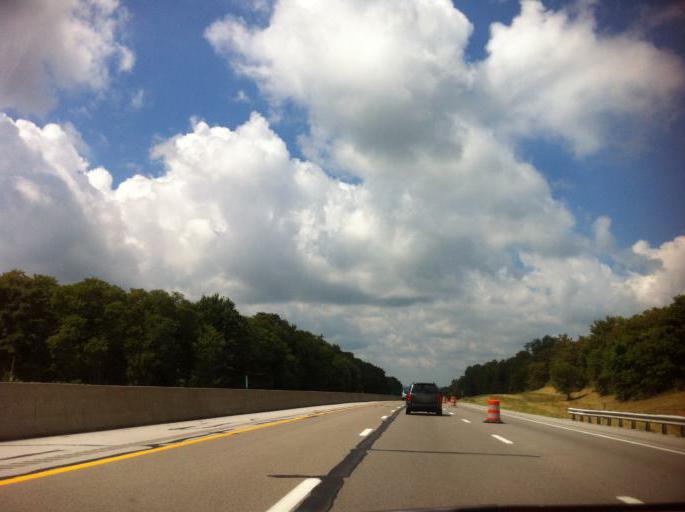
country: US
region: Ohio
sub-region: Erie County
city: Huron
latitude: 41.3290
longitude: -82.4831
